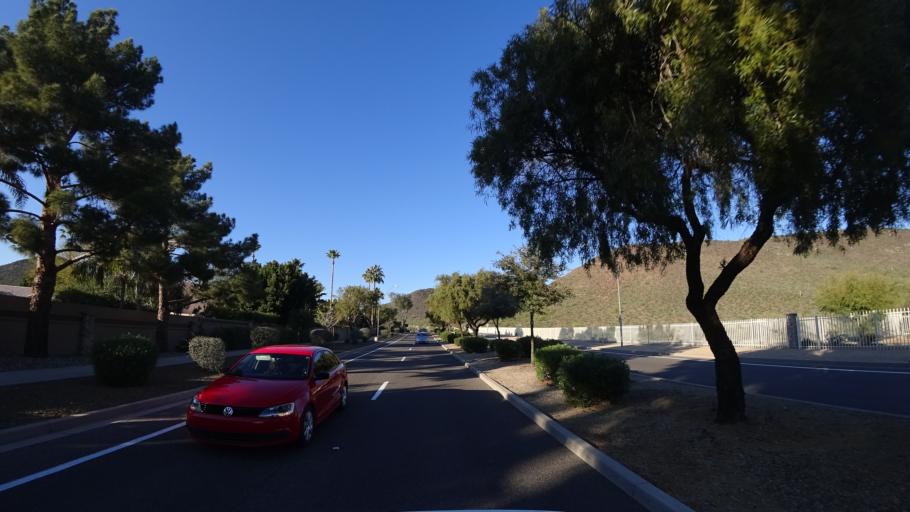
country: US
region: Arizona
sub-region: Maricopa County
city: Peoria
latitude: 33.6843
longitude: -112.1867
